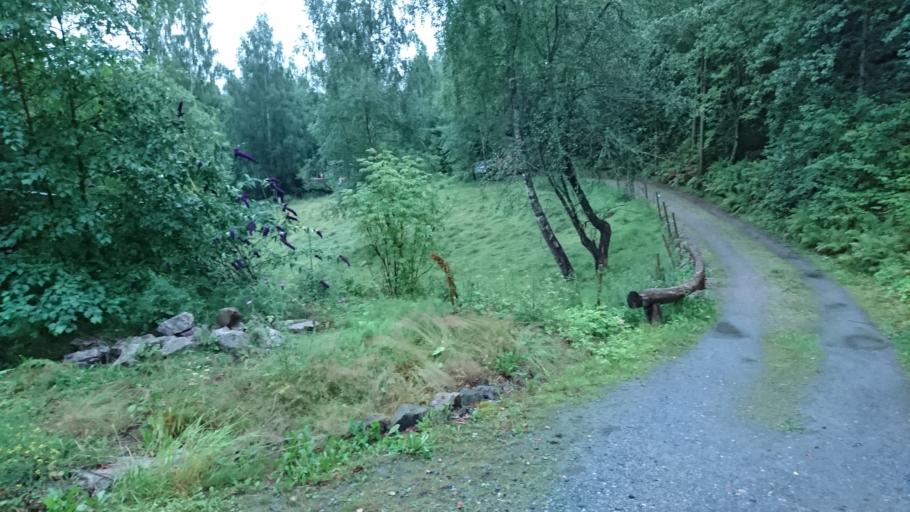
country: NO
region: Telemark
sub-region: Nome
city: Ulefoss
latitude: 59.2753
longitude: 9.3475
